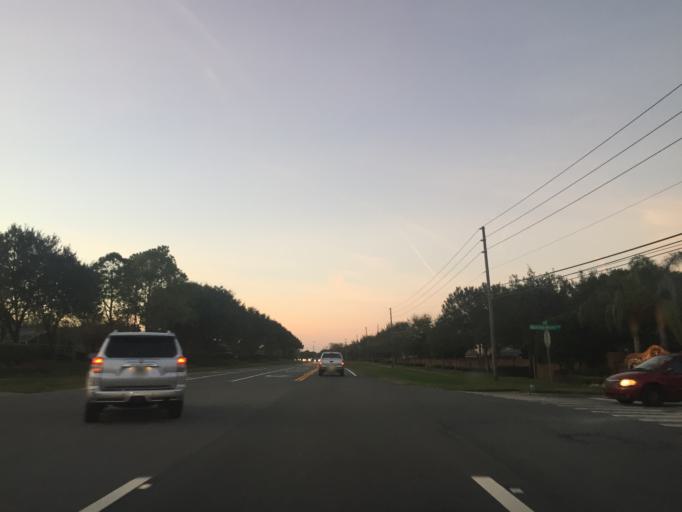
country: US
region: Florida
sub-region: Seminole County
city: Oviedo
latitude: 28.6635
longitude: -81.1823
